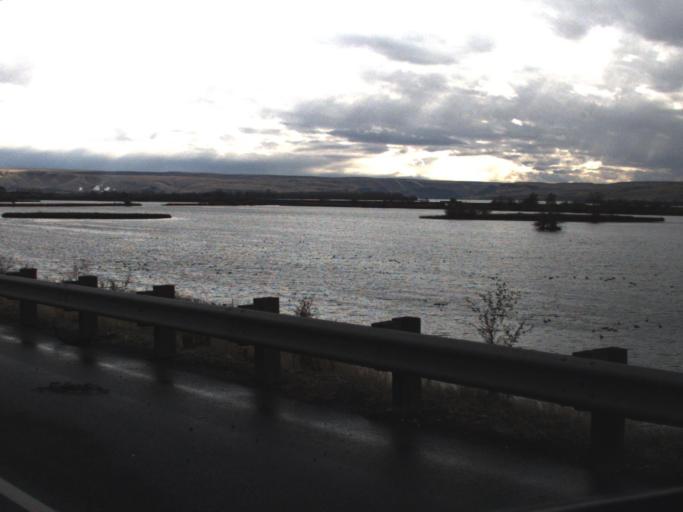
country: US
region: Washington
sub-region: Walla Walla County
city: Burbank
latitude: 46.1670
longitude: -118.9521
